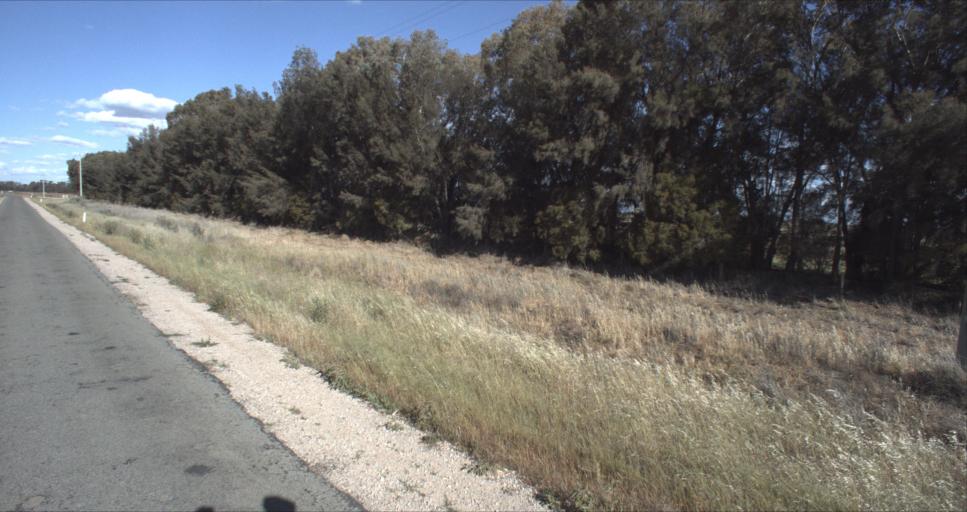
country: AU
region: New South Wales
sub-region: Leeton
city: Leeton
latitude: -34.4585
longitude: 146.2669
